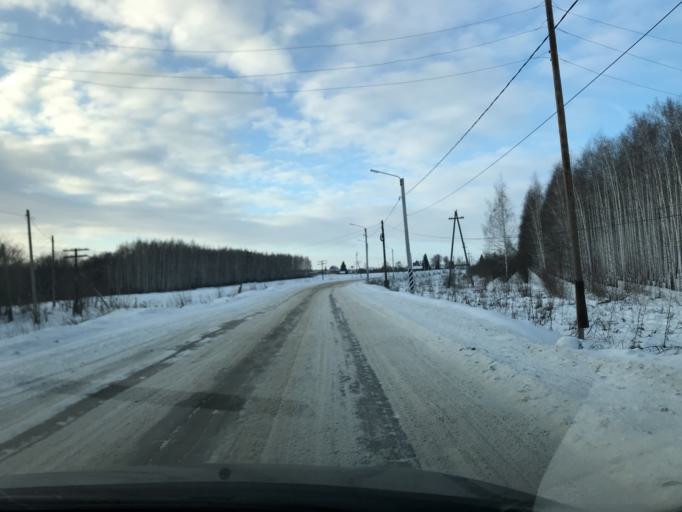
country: RU
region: Ulyanovsk
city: Undory
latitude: 54.6020
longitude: 48.4201
